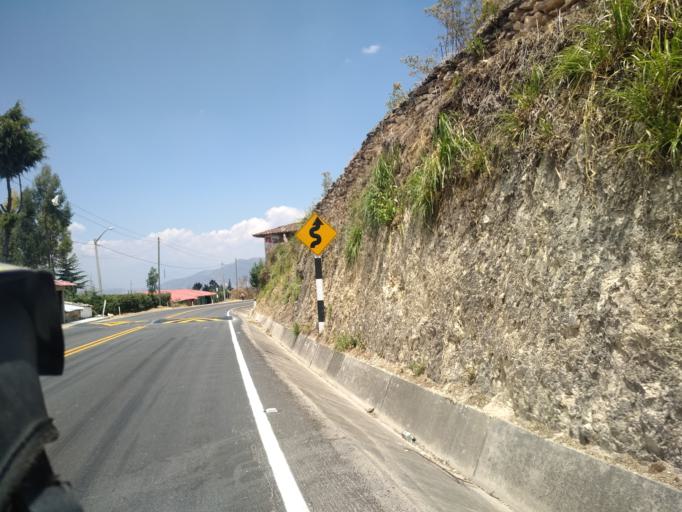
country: PE
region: Cajamarca
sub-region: San Marcos
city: San Marcos
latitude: -7.2776
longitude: -78.2419
